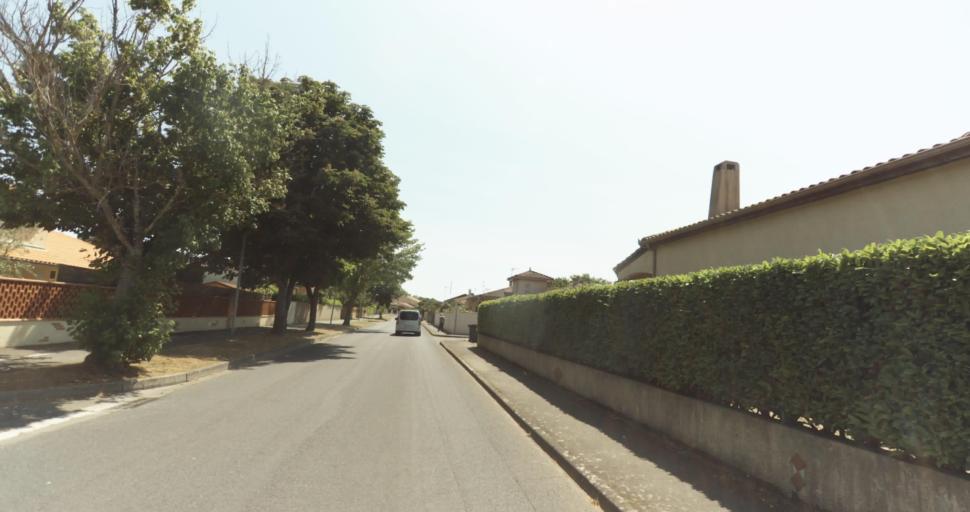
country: FR
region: Midi-Pyrenees
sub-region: Departement de la Haute-Garonne
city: Plaisance-du-Touch
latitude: 43.5627
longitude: 1.3076
